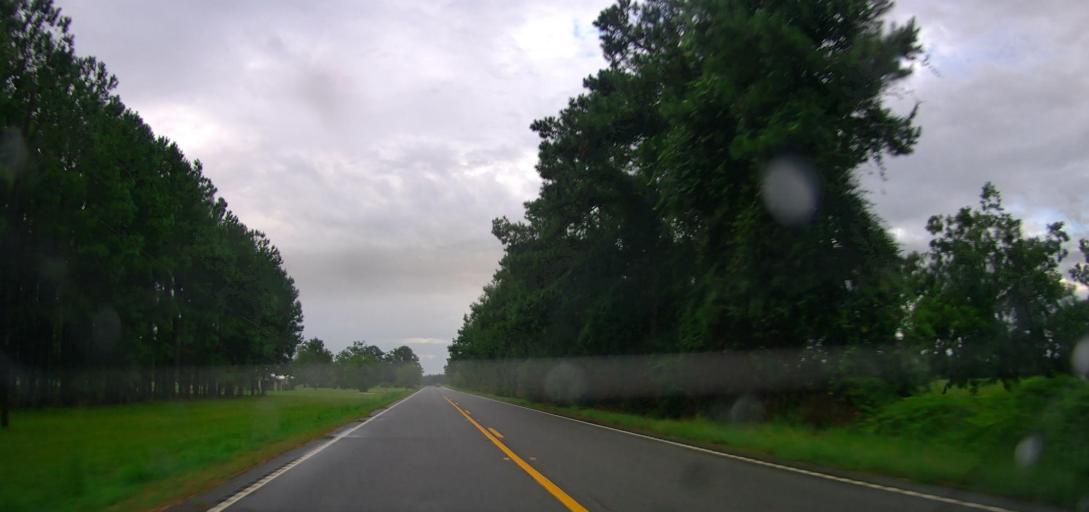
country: US
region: Georgia
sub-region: Ware County
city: Deenwood
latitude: 31.2682
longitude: -82.4003
